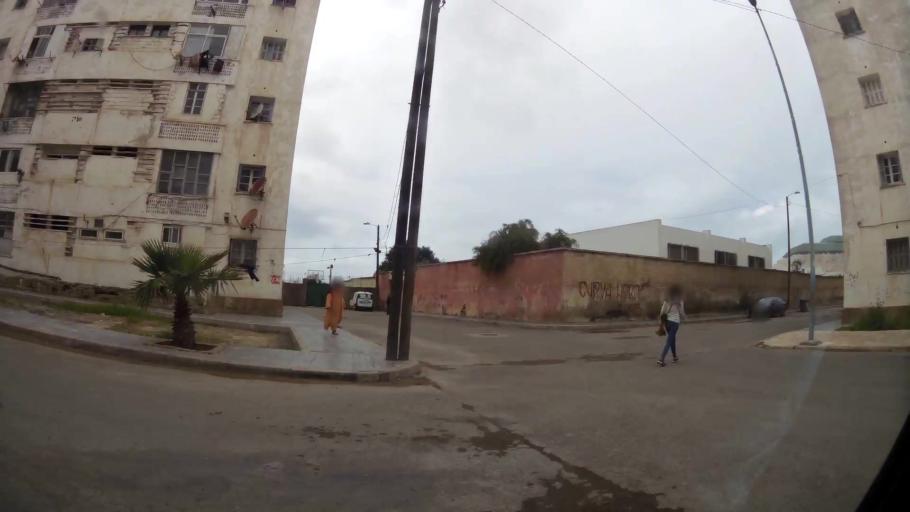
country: MA
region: Grand Casablanca
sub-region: Casablanca
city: Casablanca
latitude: 33.6042
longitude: -7.6359
